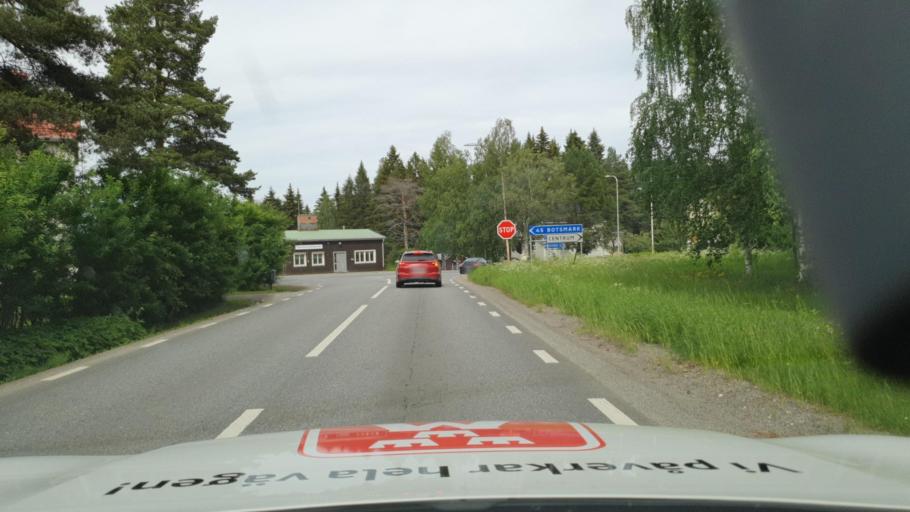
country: SE
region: Vaesterbotten
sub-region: Skelleftea Kommun
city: Burtraesk
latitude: 64.5116
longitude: 20.6346
